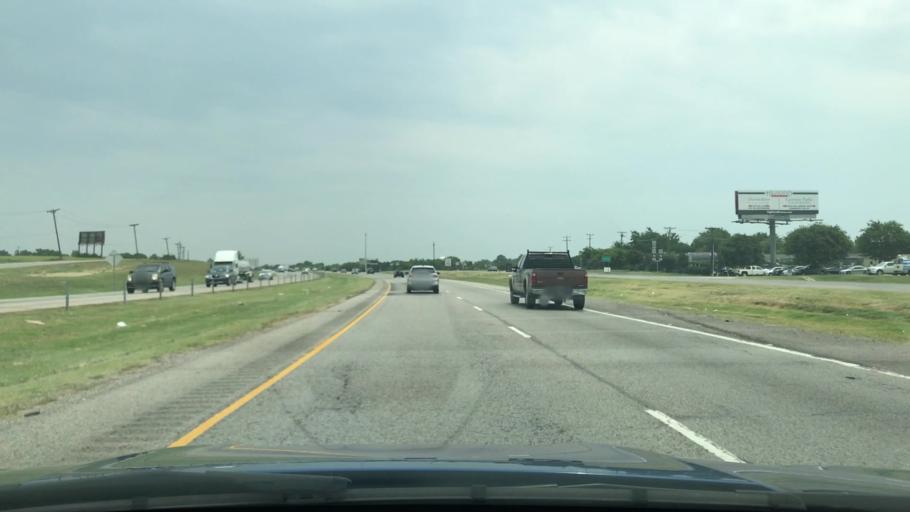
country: US
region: Texas
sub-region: Kaufman County
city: Forney
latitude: 32.7627
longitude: -96.4818
